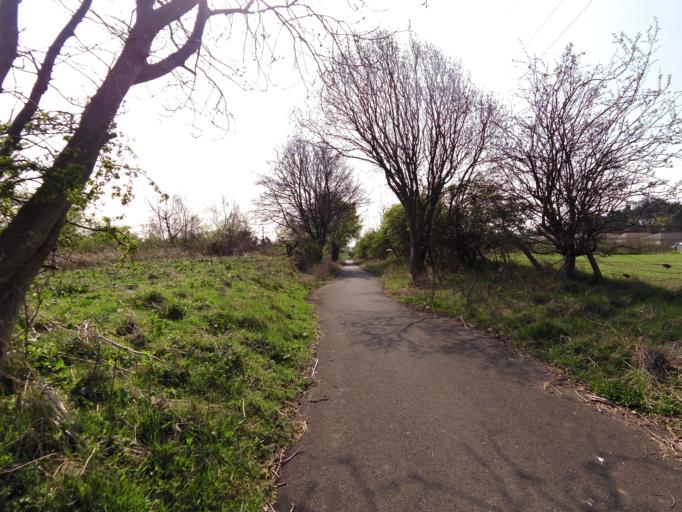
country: GB
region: Scotland
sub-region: Fife
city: Kirkcaldy
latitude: 56.1399
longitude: -3.1512
